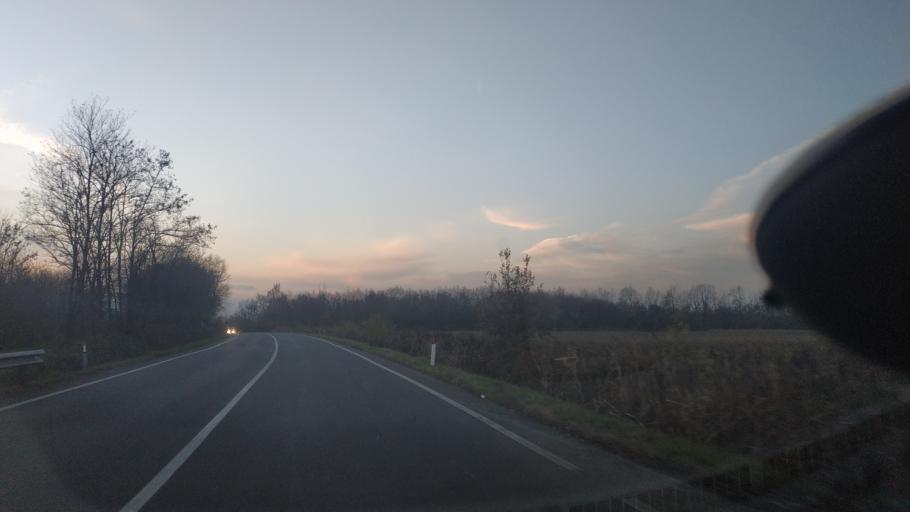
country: IT
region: Piedmont
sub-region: Provincia di Torino
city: Montanaro
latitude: 45.2432
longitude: 7.8541
